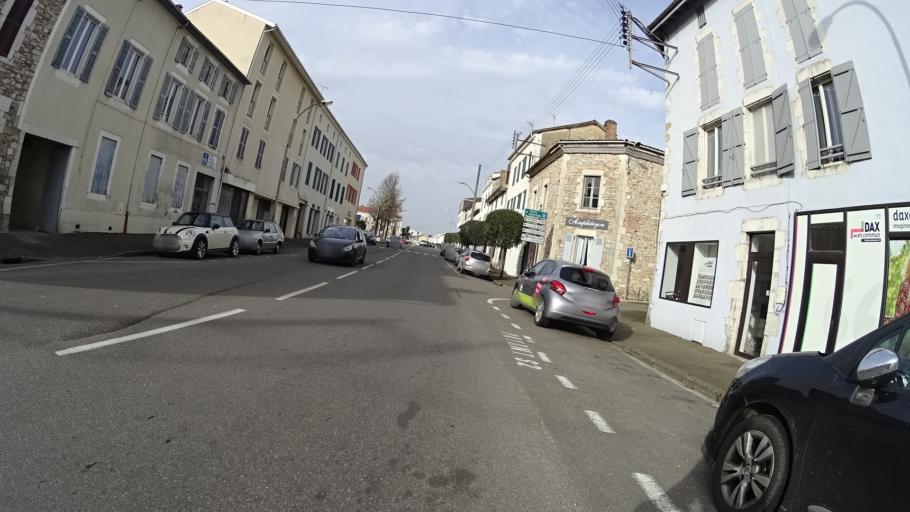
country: FR
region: Aquitaine
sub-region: Departement des Landes
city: Dax
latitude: 43.7077
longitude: -1.0502
